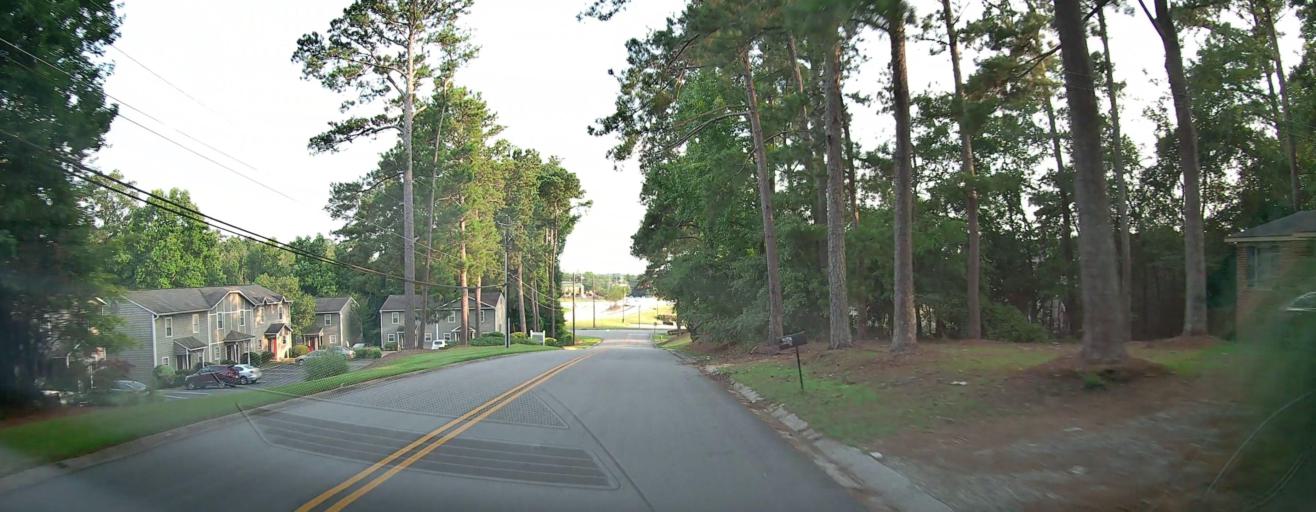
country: US
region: Georgia
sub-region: Bibb County
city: West Point
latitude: 32.8151
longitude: -83.7203
